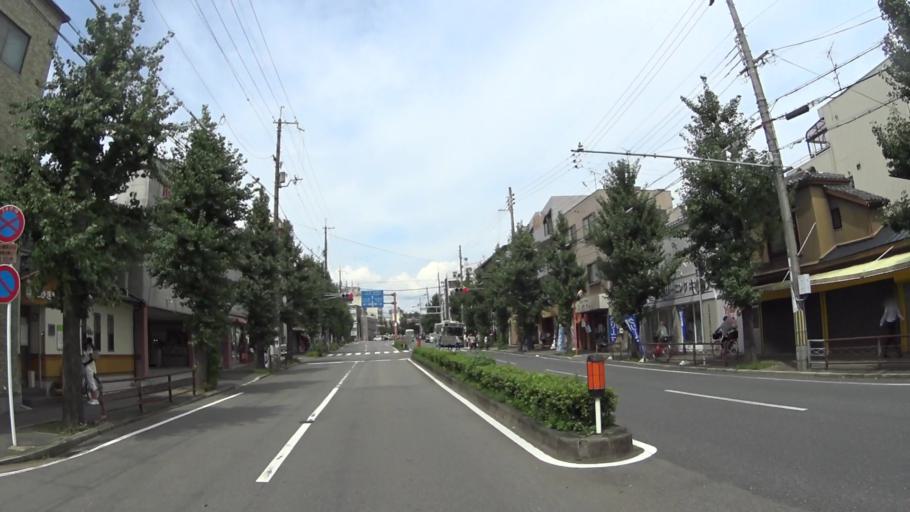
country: JP
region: Kyoto
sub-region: Kyoto-shi
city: Kamigyo-ku
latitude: 35.0262
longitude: 135.7917
